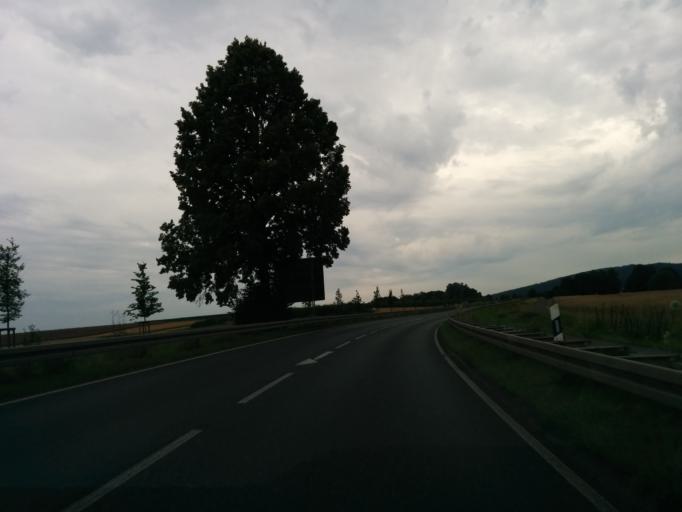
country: DE
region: Hesse
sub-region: Regierungsbezirk Kassel
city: Jesberg
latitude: 51.0492
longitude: 9.1800
